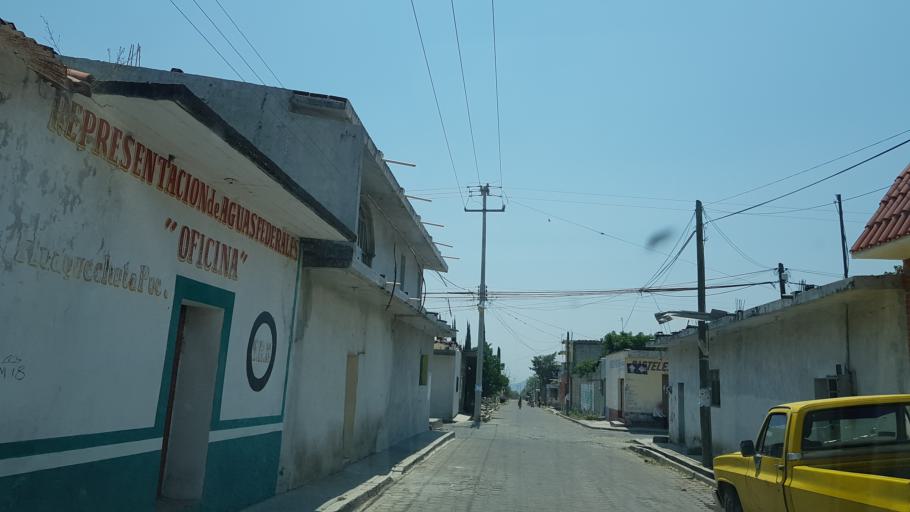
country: MX
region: Puebla
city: Huaquechula
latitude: 18.7716
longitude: -98.5460
